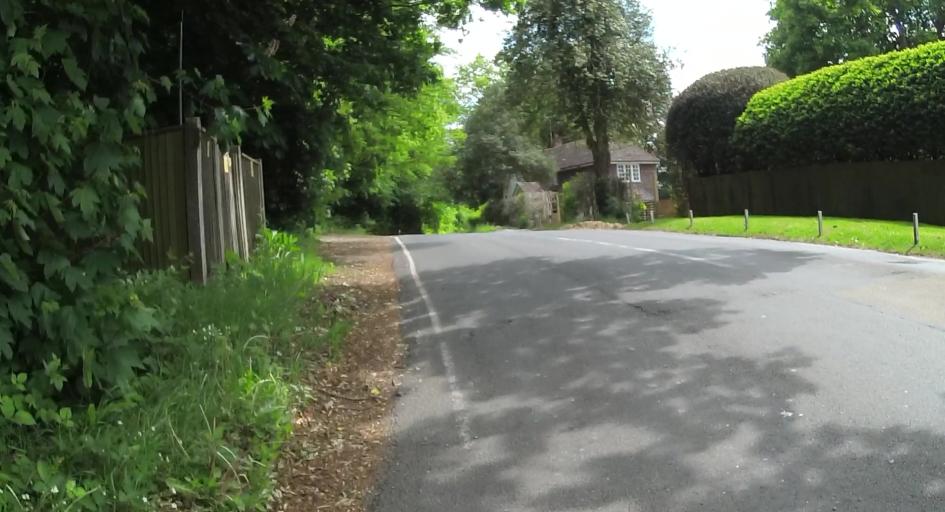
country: GB
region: England
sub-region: Surrey
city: Farnham
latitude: 51.2357
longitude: -0.8335
